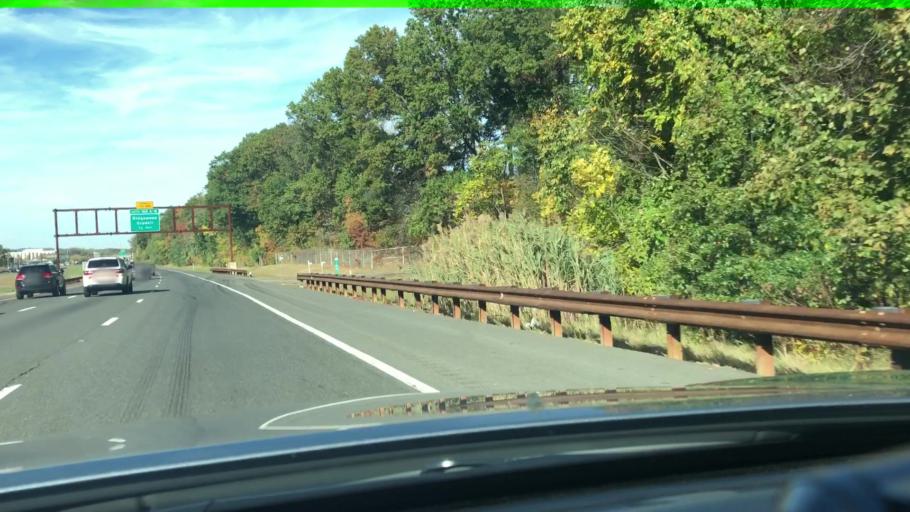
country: US
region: New Jersey
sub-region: Bergen County
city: Paramus
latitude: 40.9512
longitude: -74.0658
